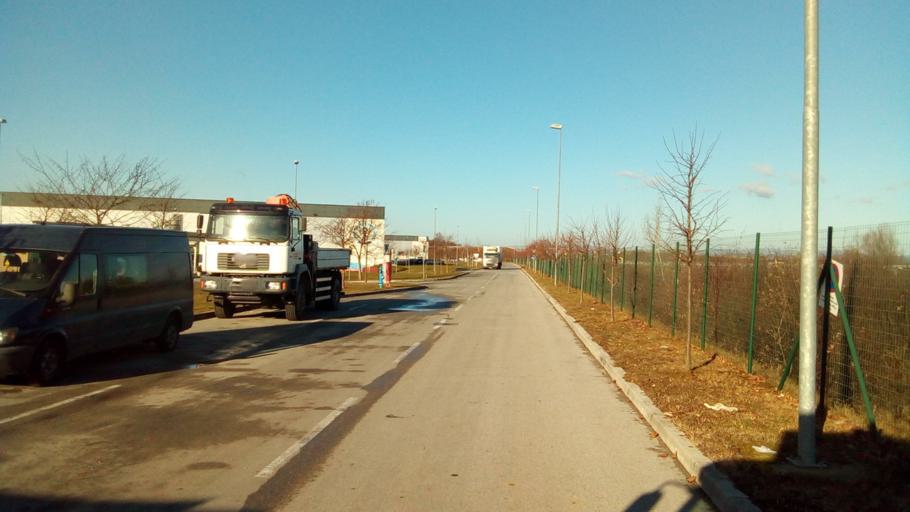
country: HR
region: Zagrebacka
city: Bestovje
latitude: 45.8039
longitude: 15.7757
